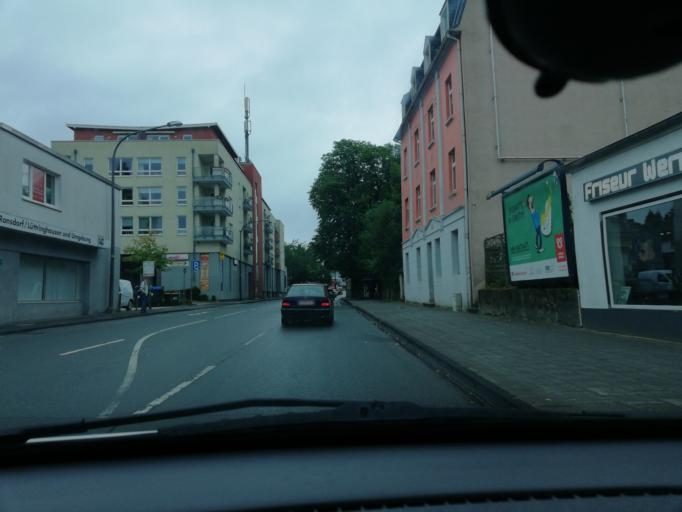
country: DE
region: North Rhine-Westphalia
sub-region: Regierungsbezirk Dusseldorf
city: Remscheid
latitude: 51.2253
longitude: 7.2004
